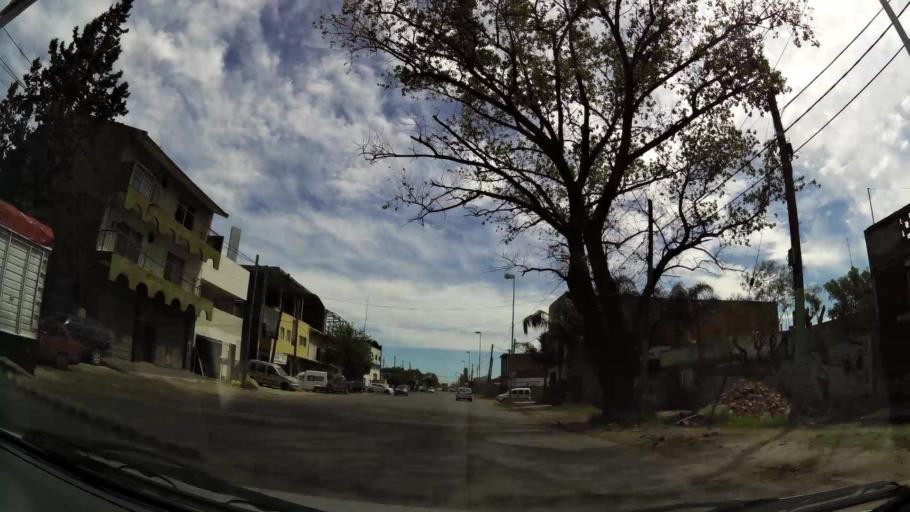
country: AR
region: Buenos Aires
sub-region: Partido de Quilmes
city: Quilmes
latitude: -34.7762
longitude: -58.2850
